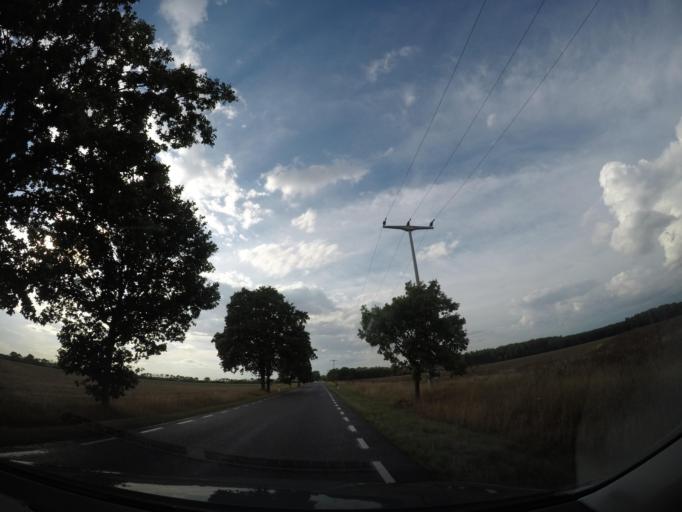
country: DE
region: Saxony-Anhalt
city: Mieste
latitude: 52.5120
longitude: 11.1716
